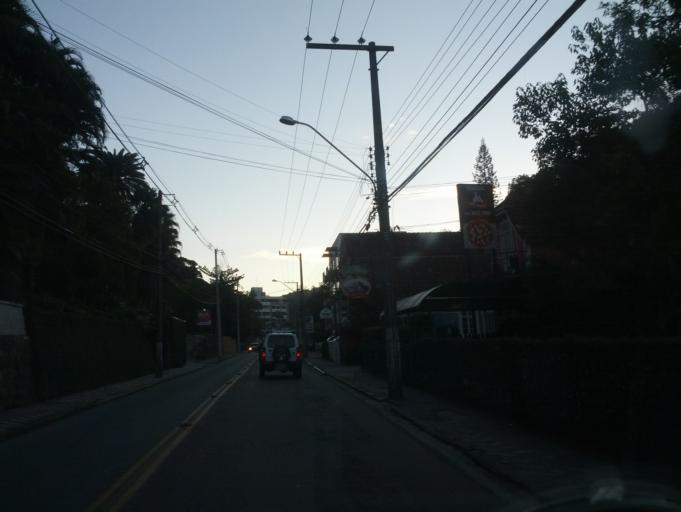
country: BR
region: Santa Catarina
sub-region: Blumenau
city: Blumenau
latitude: -26.9254
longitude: -49.0704
